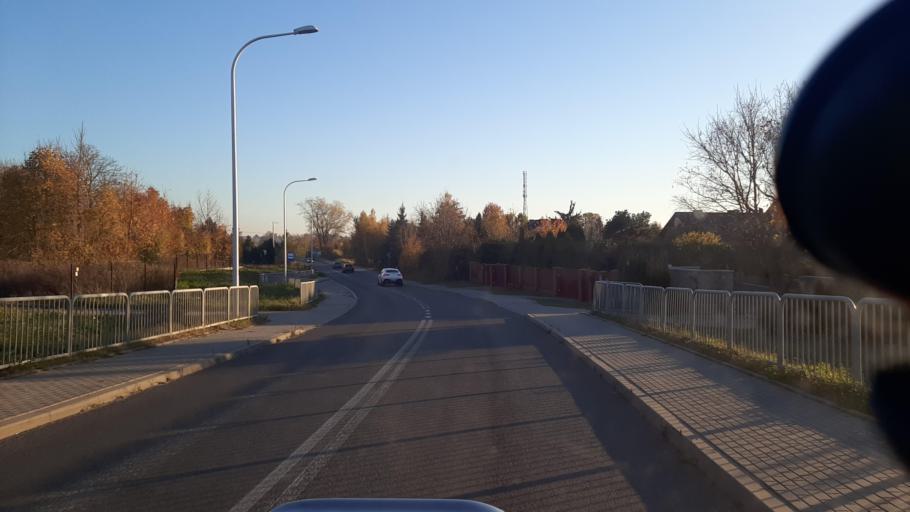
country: PL
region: Lublin Voivodeship
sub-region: Powiat lubelski
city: Lublin
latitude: 51.2963
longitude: 22.5420
